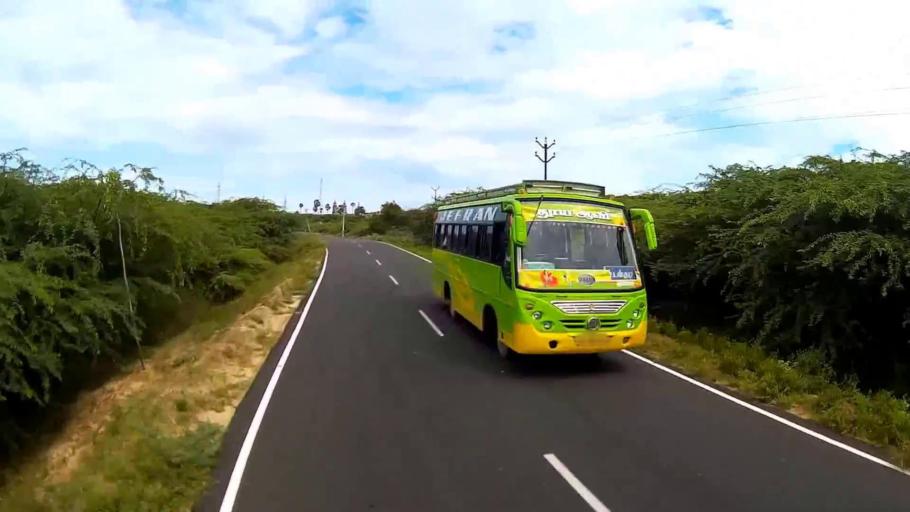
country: IN
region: Tamil Nadu
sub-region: Thoothukkudi
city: Udankudi
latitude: 8.3804
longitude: 78.0492
